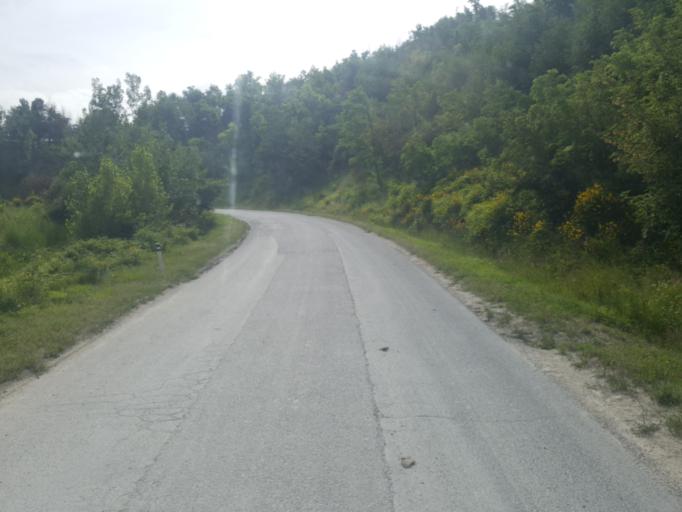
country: IT
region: Emilia-Romagna
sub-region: Provincia di Piacenza
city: Ponte dell'Olio
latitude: 44.8724
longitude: 9.6180
